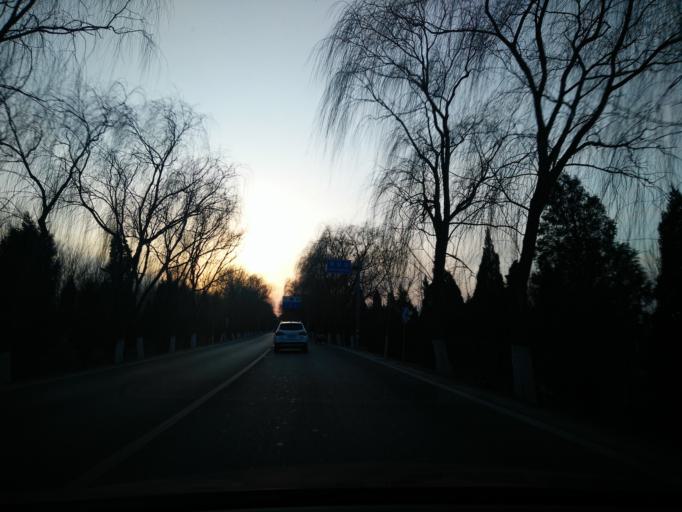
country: CN
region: Beijing
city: Qingyundian
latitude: 39.6730
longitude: 116.5152
